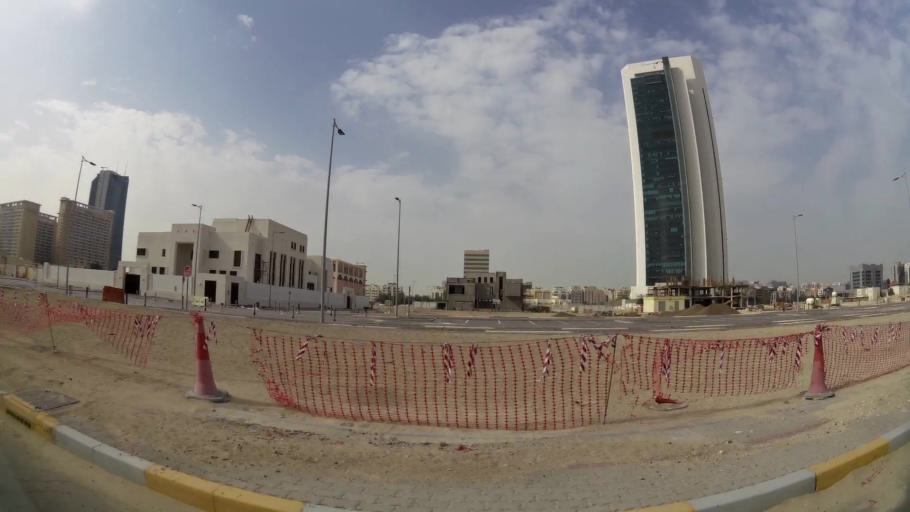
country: AE
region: Abu Dhabi
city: Abu Dhabi
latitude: 24.4609
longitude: 54.3948
